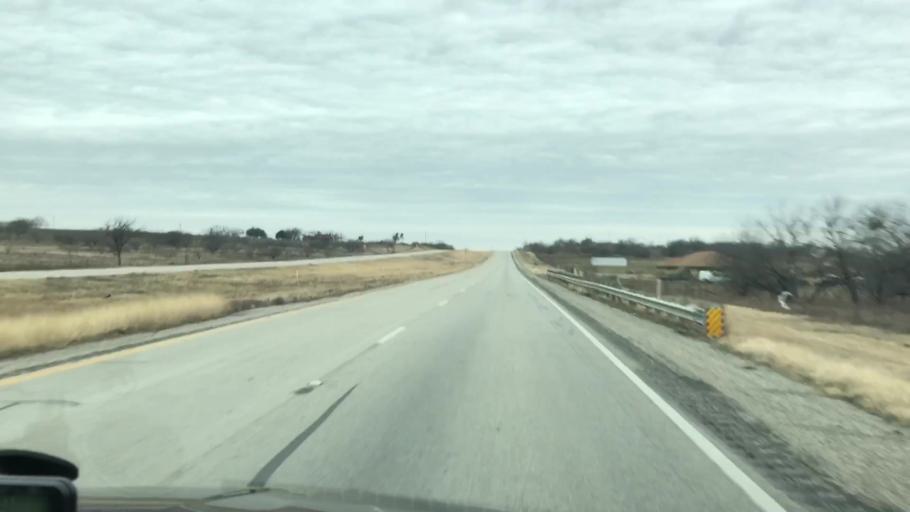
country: US
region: Texas
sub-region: Jack County
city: Jacksboro
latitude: 33.2417
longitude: -98.2210
